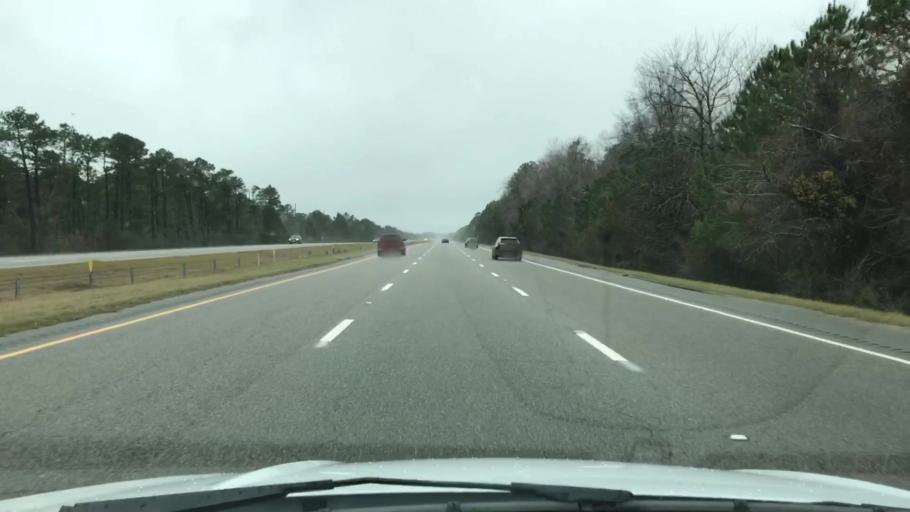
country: US
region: South Carolina
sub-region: Horry County
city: Forestbrook
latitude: 33.7493
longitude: -78.9040
